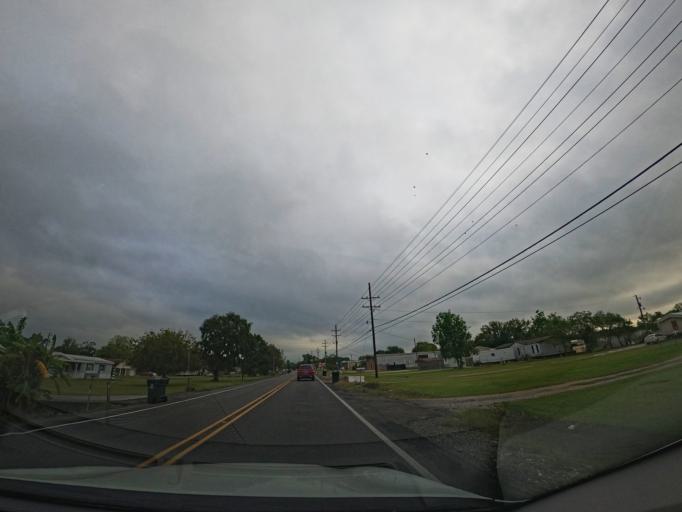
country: US
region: Louisiana
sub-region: Terrebonne Parish
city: Presquille
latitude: 29.5028
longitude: -90.6769
